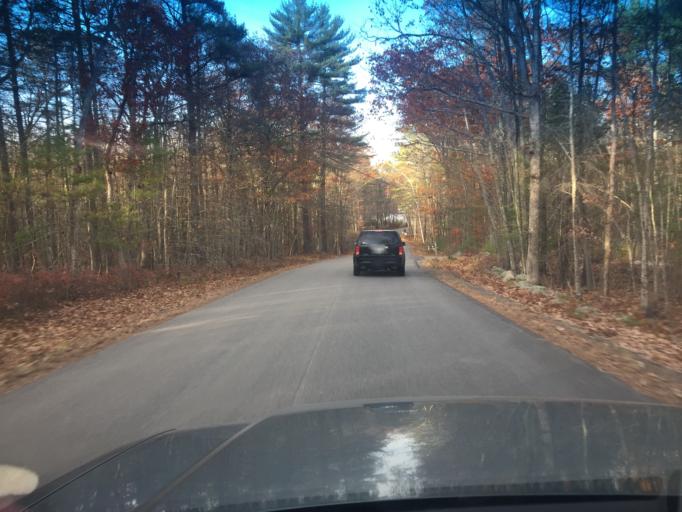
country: US
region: Maine
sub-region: York County
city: Eliot
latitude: 43.1933
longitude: -70.7483
